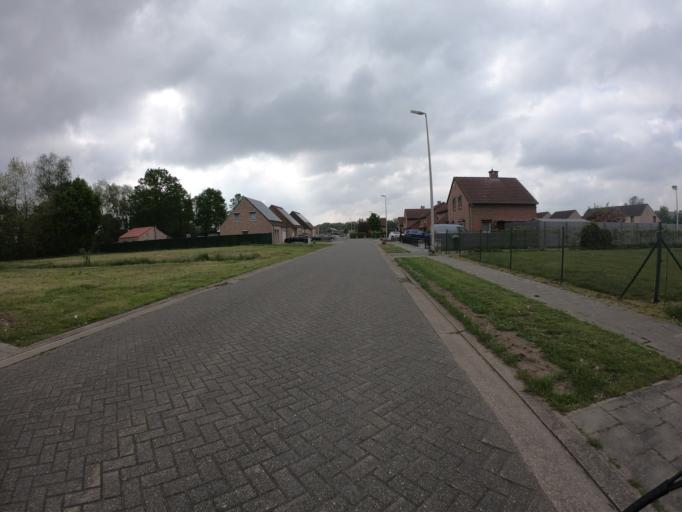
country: BE
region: Flanders
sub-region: Provincie Limburg
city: Genk
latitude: 50.9291
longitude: 5.4694
